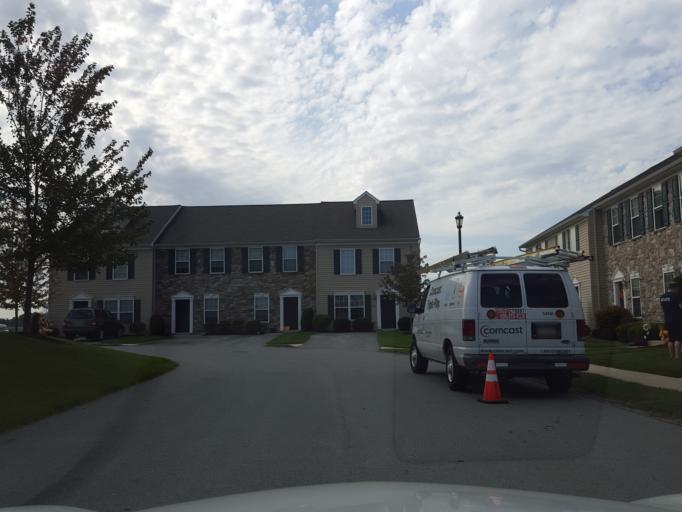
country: US
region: Pennsylvania
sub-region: York County
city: Yoe
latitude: 39.9206
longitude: -76.6272
